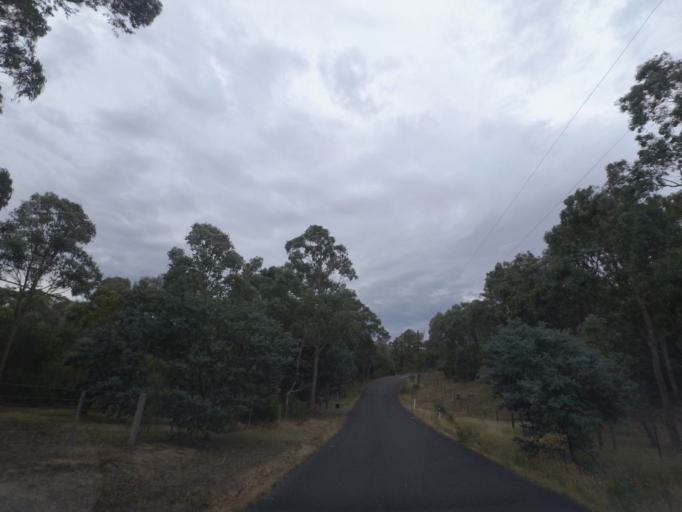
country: AU
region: Victoria
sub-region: Nillumbik
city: Diamond Creek
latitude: -37.6606
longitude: 145.1334
